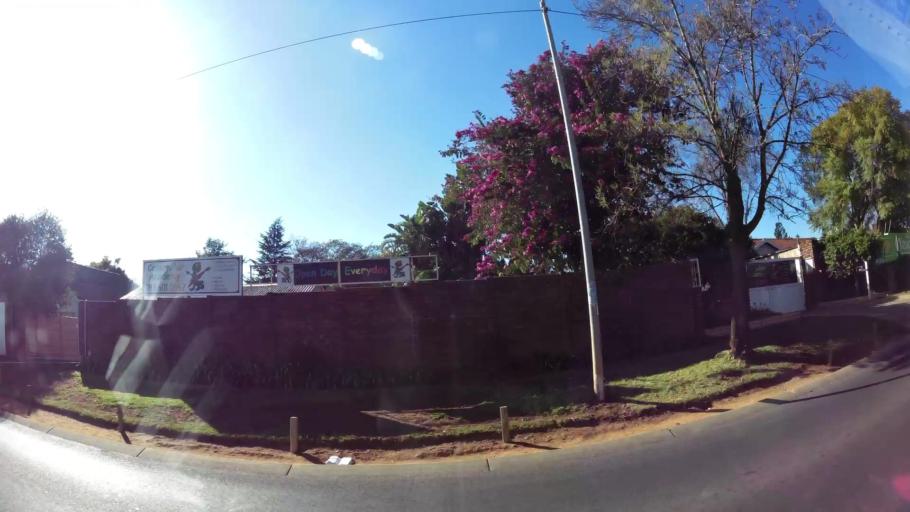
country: ZA
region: Gauteng
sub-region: City of Johannesburg Metropolitan Municipality
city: Diepsloot
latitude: -26.0532
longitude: 27.9740
